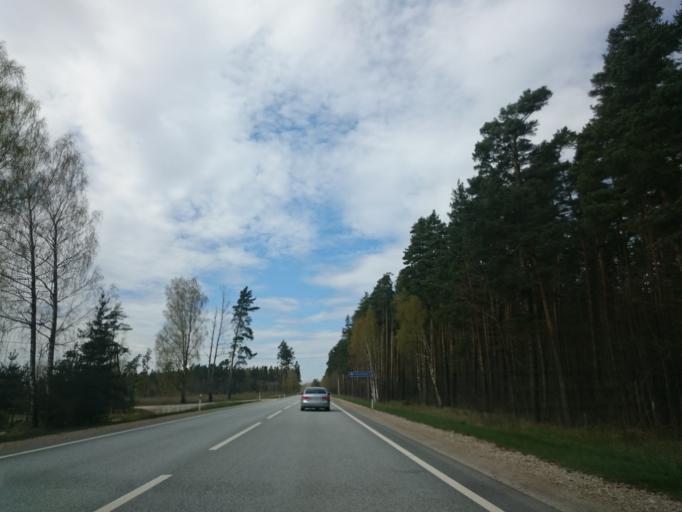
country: LV
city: Tireli
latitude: 56.9277
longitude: 23.6583
